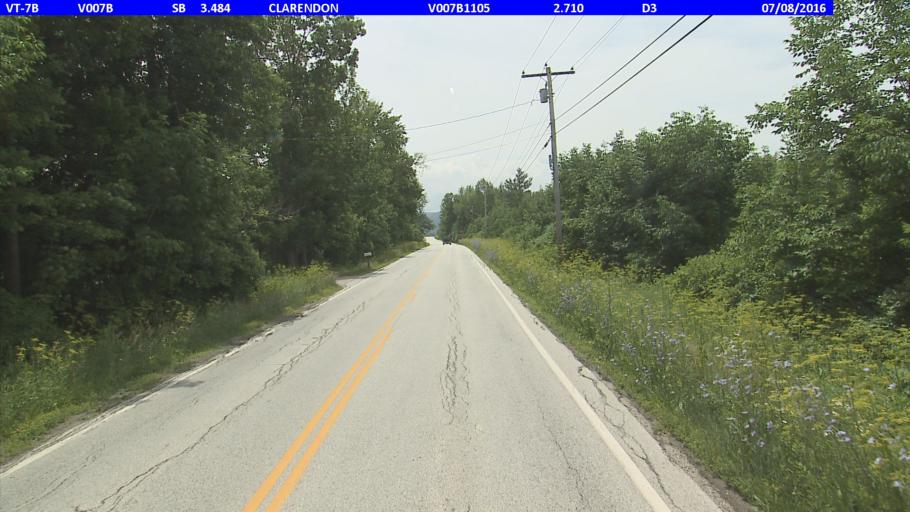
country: US
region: Vermont
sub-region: Rutland County
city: Rutland
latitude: 43.5383
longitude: -72.9535
